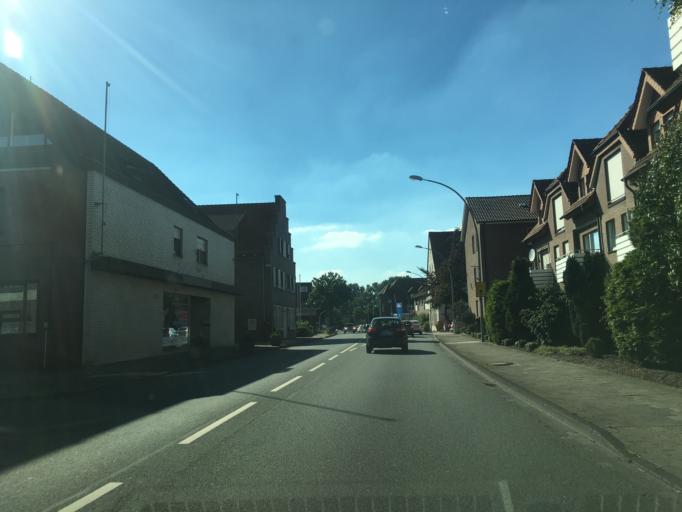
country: DE
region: North Rhine-Westphalia
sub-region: Regierungsbezirk Munster
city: Beelen
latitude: 51.9303
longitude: 8.1160
